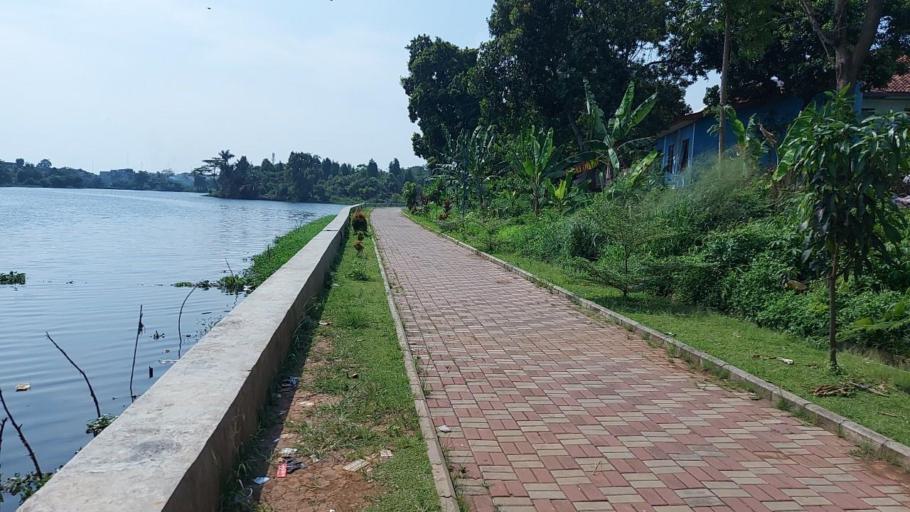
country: ID
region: West Java
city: Cibinong
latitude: -6.4705
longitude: 106.8545
